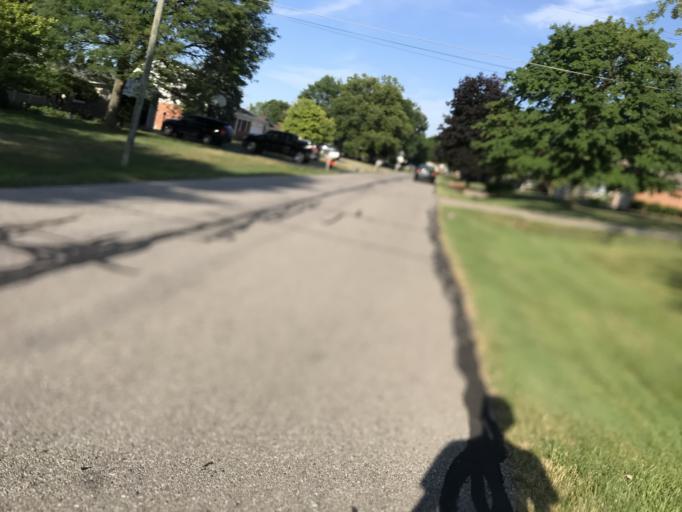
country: US
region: Michigan
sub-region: Oakland County
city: Farmington Hills
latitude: 42.4843
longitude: -83.3357
